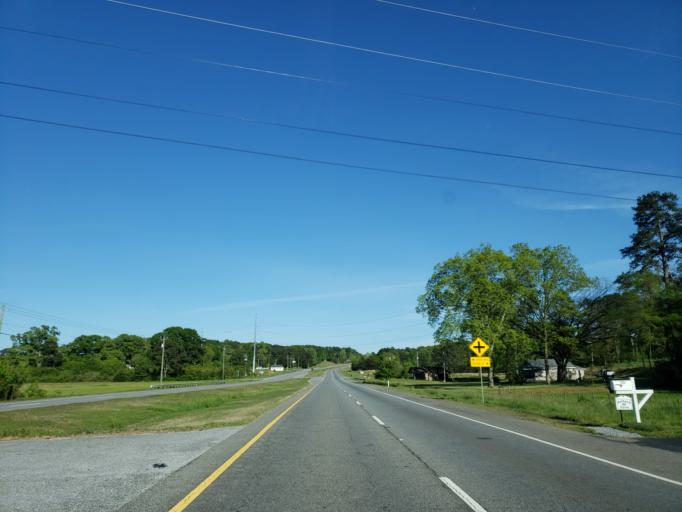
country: US
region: Georgia
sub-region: Polk County
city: Cedartown
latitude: 34.0143
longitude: -85.1921
